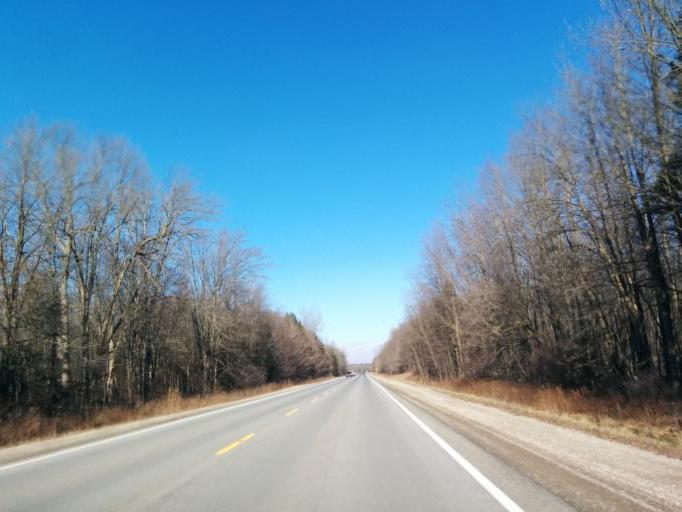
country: CA
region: Ontario
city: Brant
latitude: 43.0429
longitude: -80.3670
